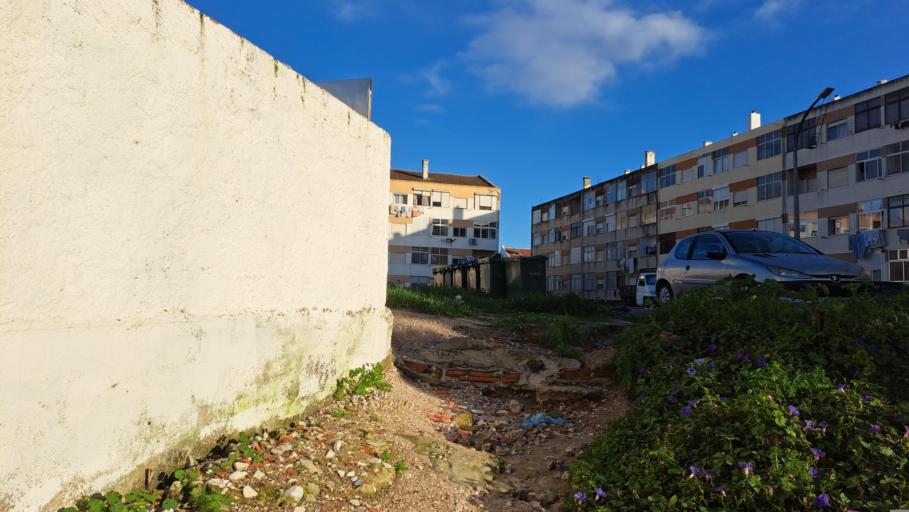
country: PT
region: Setubal
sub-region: Moita
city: Alhos Vedros
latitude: 38.6478
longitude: -9.0379
